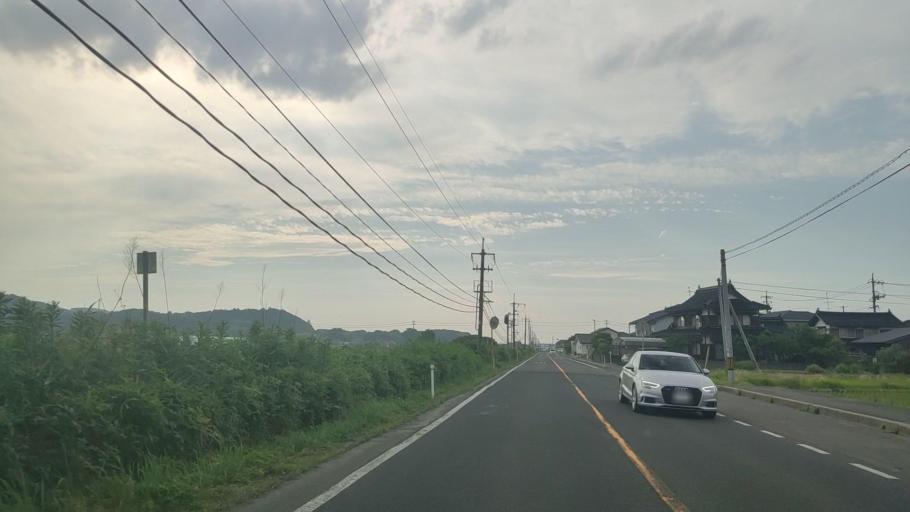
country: JP
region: Tottori
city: Kurayoshi
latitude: 35.4743
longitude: 133.8233
